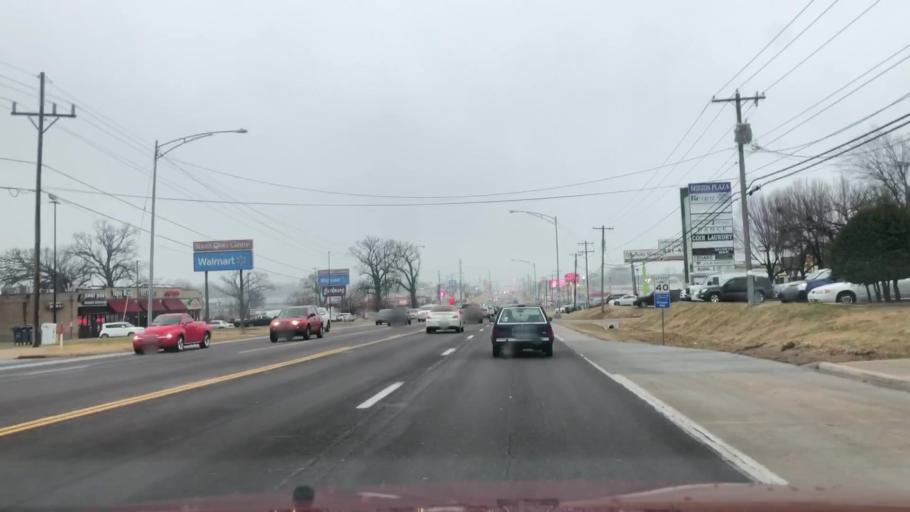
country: US
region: Missouri
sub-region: Greene County
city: Springfield
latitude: 37.1531
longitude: -93.2958
